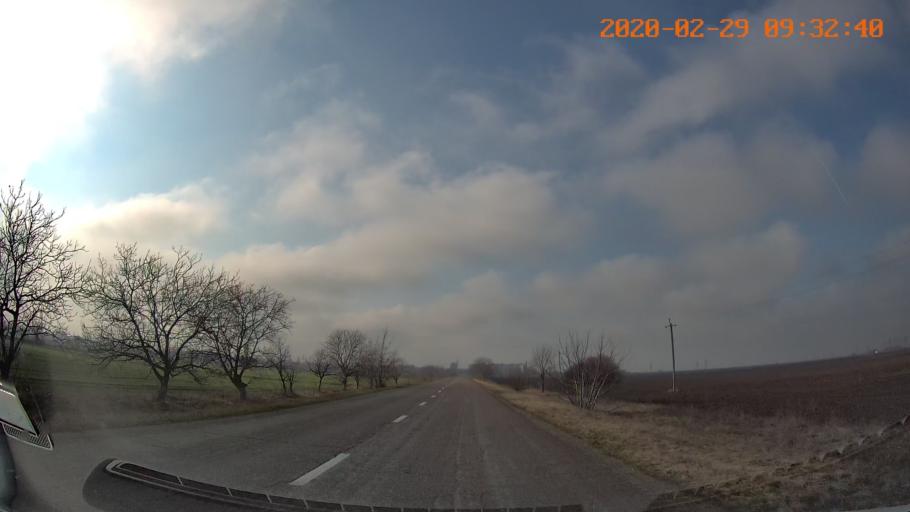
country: MD
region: Telenesti
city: Dnestrovsc
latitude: 46.6364
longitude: 29.9048
